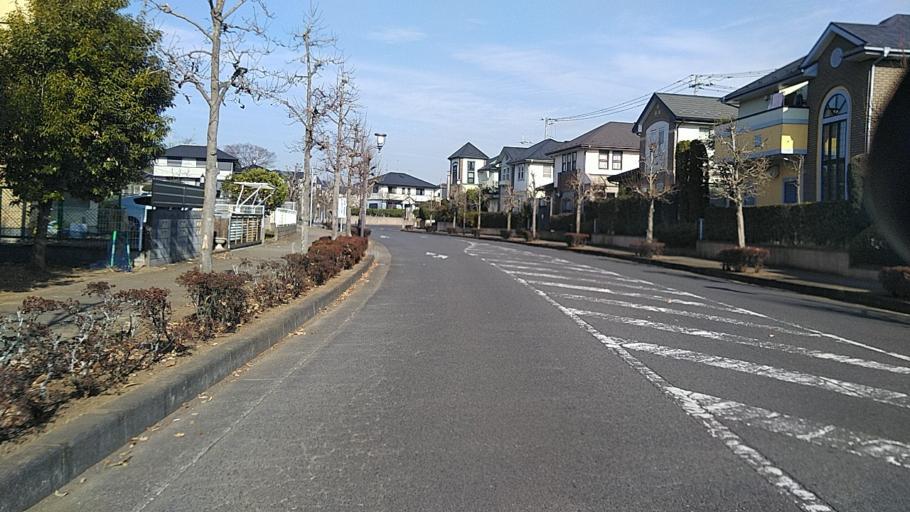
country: JP
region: Ibaraki
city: Moriya
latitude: 35.9268
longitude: 140.0012
